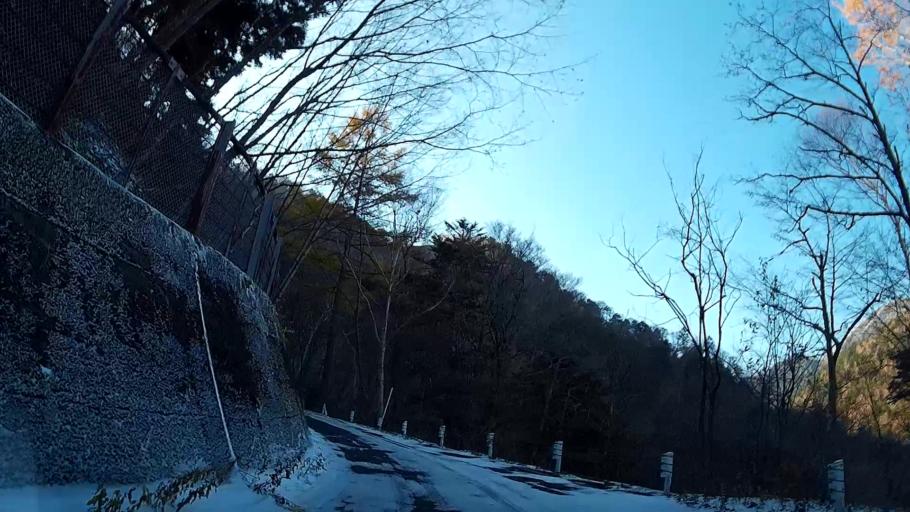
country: JP
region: Nagano
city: Hotaka
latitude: 36.2034
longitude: 137.6002
